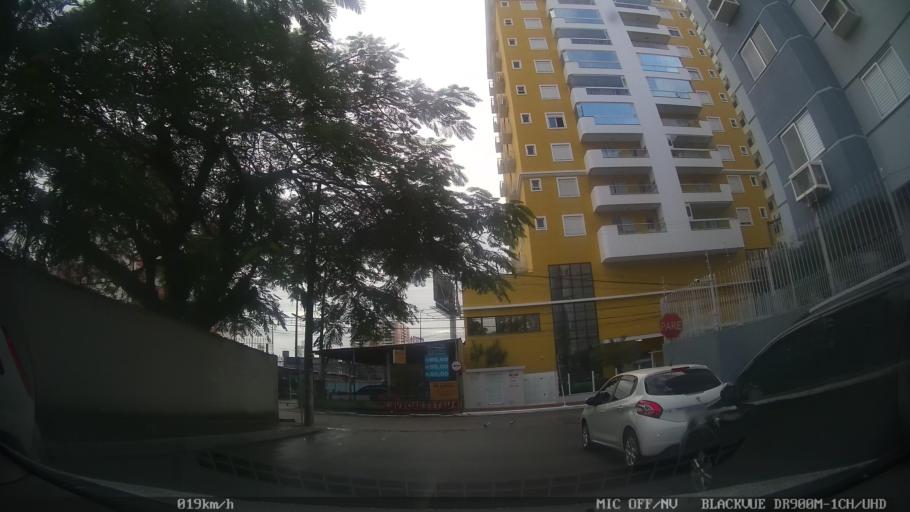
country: BR
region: Santa Catarina
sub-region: Sao Jose
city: Campinas
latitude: -27.5907
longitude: -48.6102
